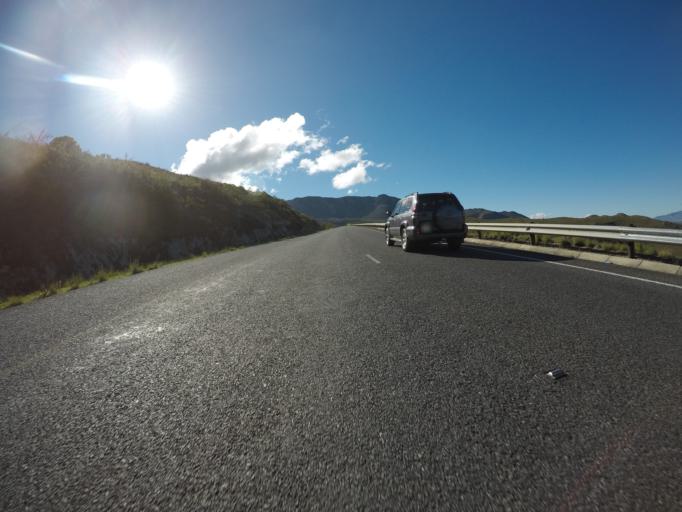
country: ZA
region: Western Cape
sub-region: Overberg District Municipality
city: Grabouw
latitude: -34.2226
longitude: 19.1720
